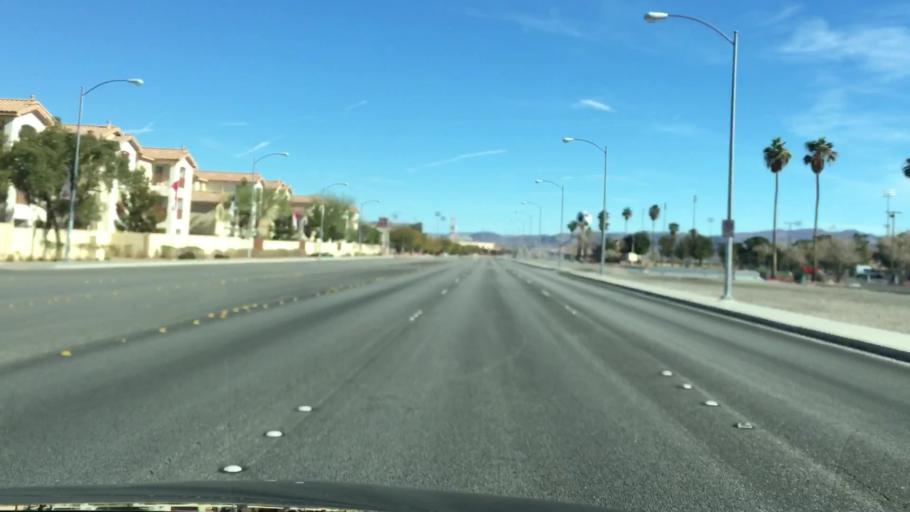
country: US
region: Nevada
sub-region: Clark County
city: Whitney
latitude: 36.0855
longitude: -115.0277
